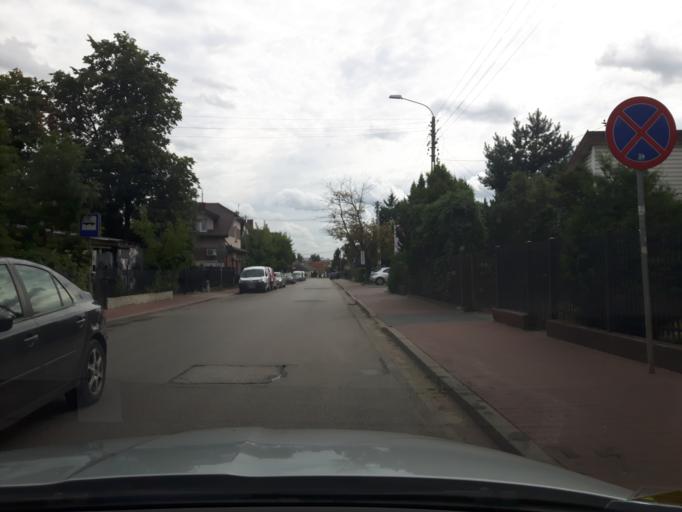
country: PL
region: Masovian Voivodeship
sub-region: Powiat wolominski
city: Zabki
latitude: 52.2901
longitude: 21.1109
